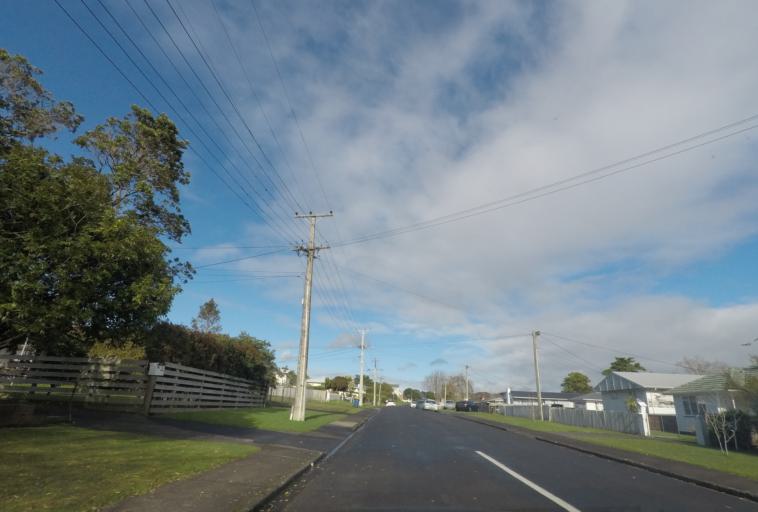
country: NZ
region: Auckland
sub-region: Auckland
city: Waitakere
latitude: -36.9013
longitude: 174.6631
